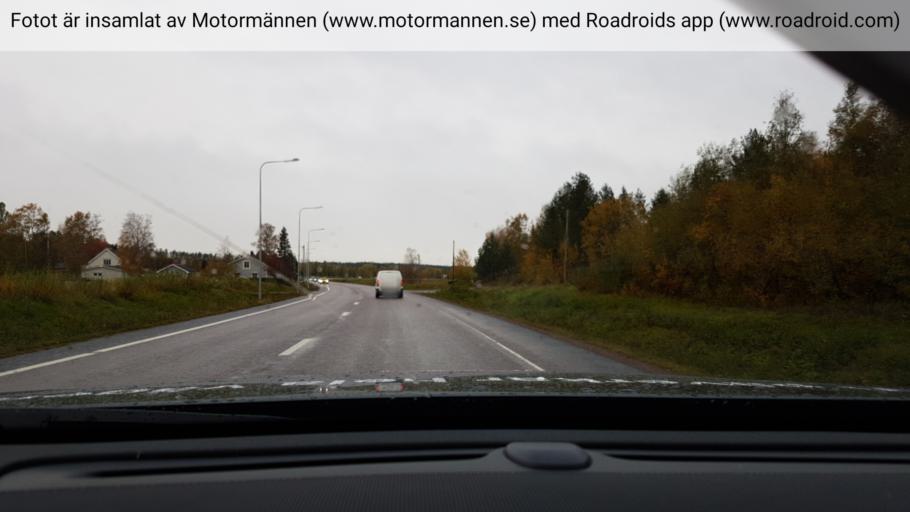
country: SE
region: Norrbotten
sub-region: Lulea Kommun
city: Bergnaset
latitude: 65.5814
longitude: 22.0558
